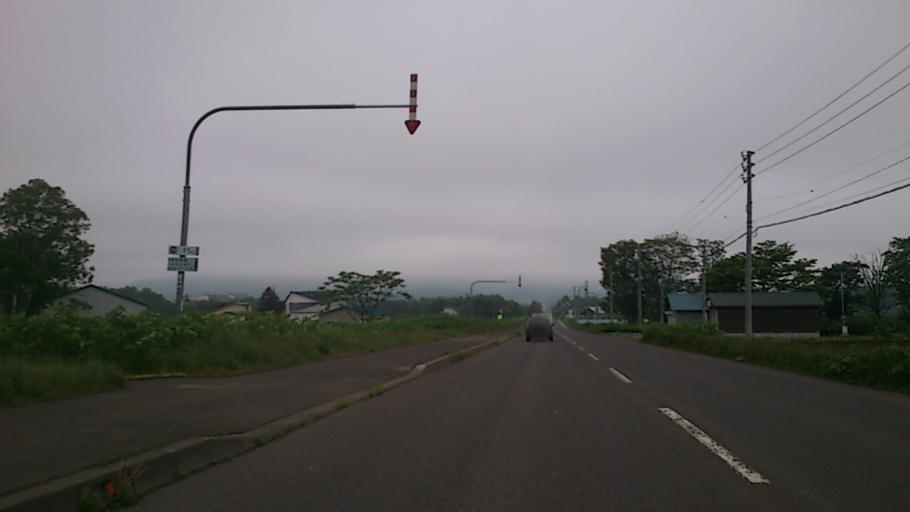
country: JP
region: Hokkaido
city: Niseko Town
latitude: 42.8832
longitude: 140.7681
